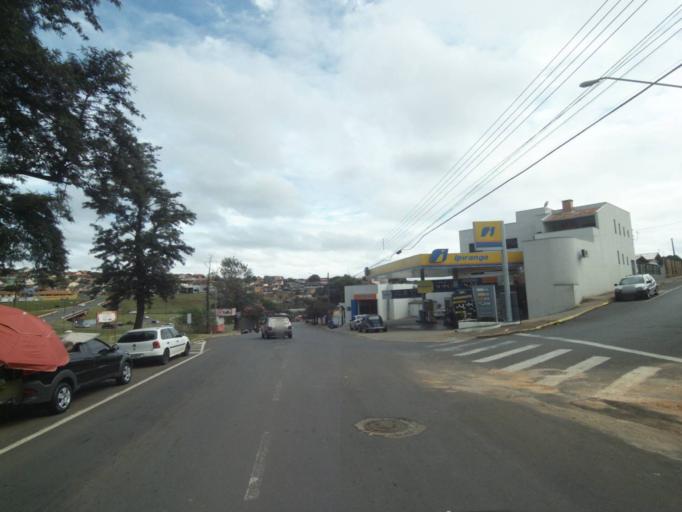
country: BR
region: Parana
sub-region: Telemaco Borba
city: Telemaco Borba
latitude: -24.3270
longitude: -50.6266
